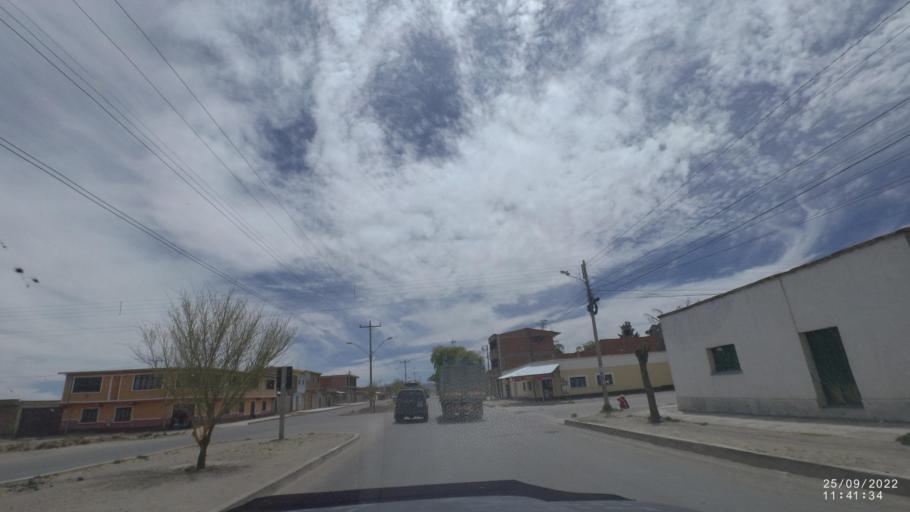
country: BO
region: Oruro
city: Challapata
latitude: -18.9043
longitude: -66.7771
